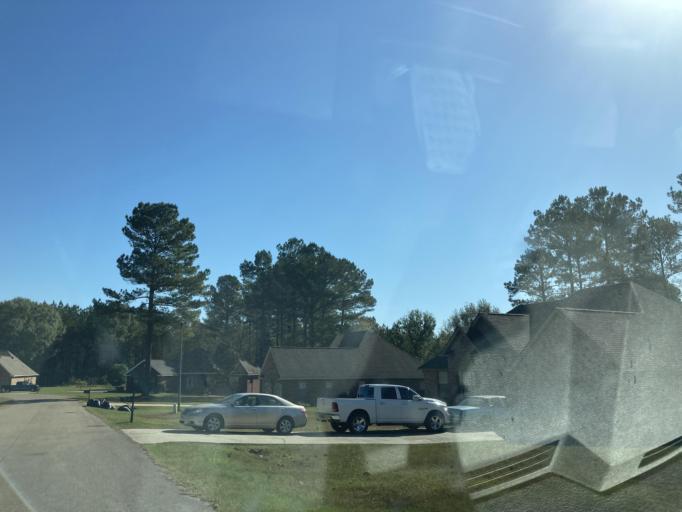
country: US
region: Mississippi
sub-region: Lamar County
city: Sumrall
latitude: 31.3485
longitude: -89.4951
